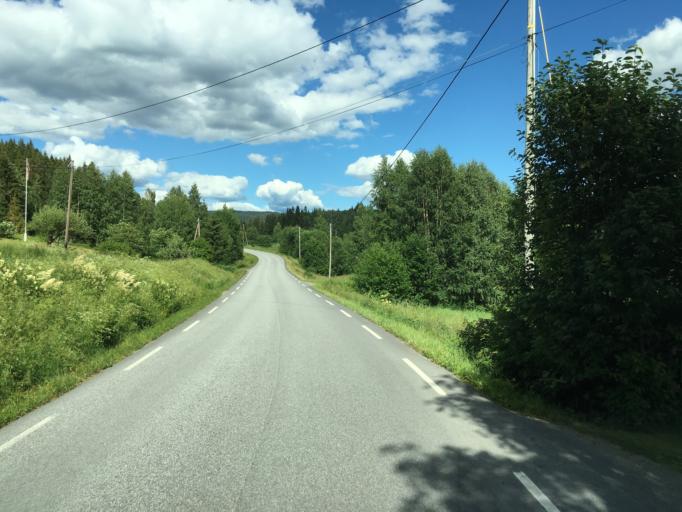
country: NO
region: Oppland
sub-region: Sondre Land
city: Hov
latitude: 60.6182
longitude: 10.3378
